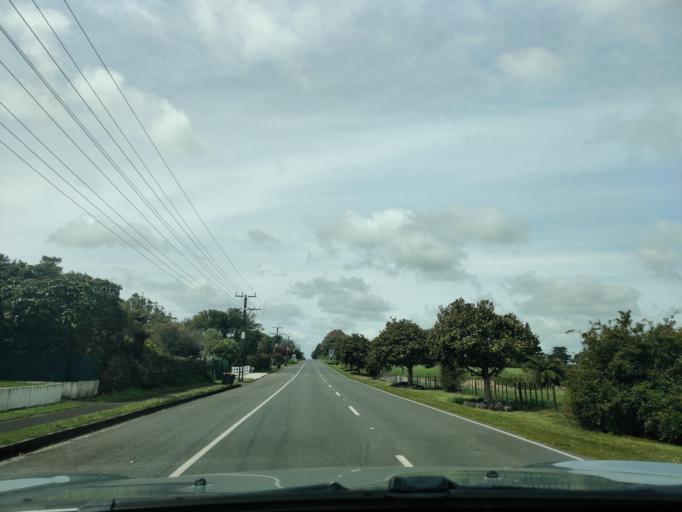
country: NZ
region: Taranaki
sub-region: South Taranaki District
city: Eltham
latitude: -39.4288
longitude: 174.1541
